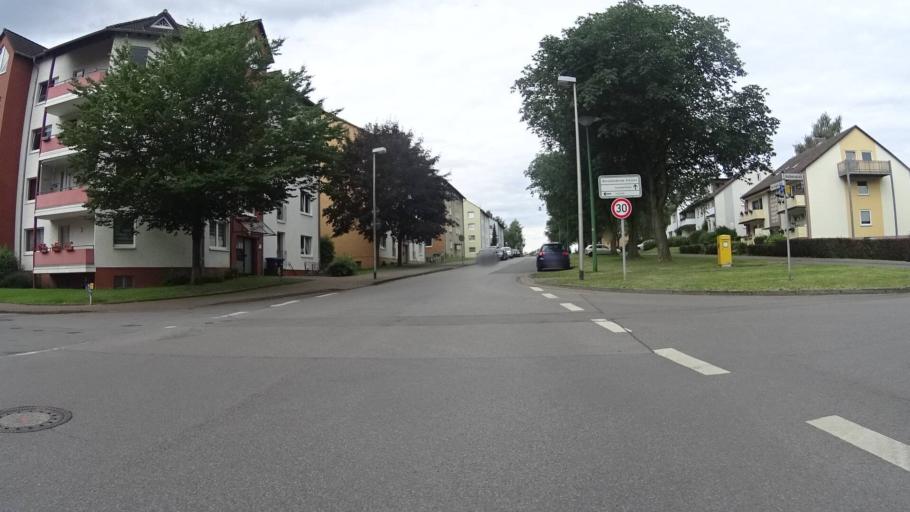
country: DE
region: Lower Saxony
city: Holzminden
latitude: 51.8199
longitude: 9.4652
